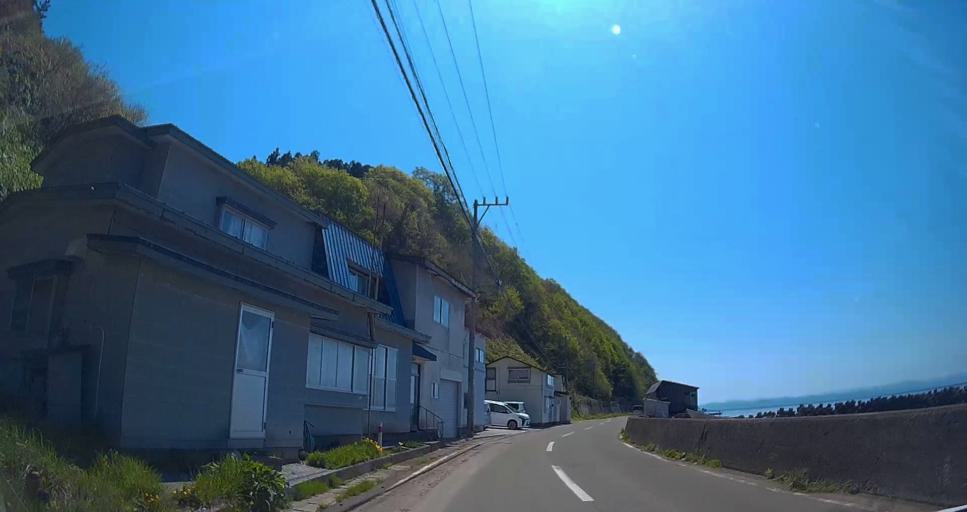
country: JP
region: Aomori
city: Aomori Shi
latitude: 41.1327
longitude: 140.7940
